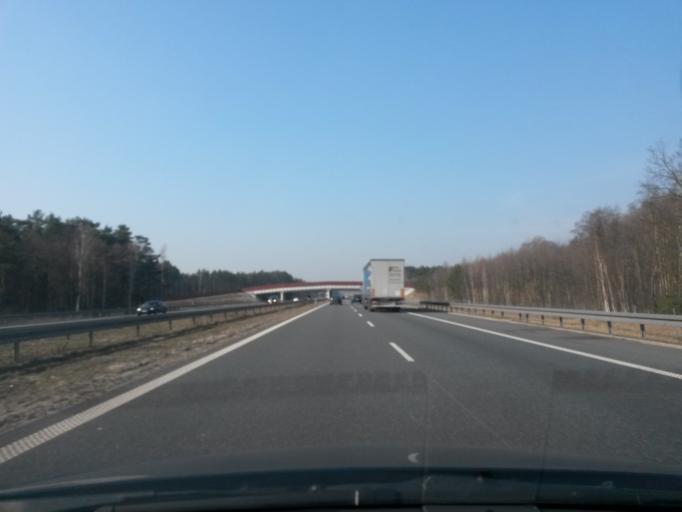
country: PL
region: Lodz Voivodeship
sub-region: Powiat skierniewicki
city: Bolimow
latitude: 52.0549
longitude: 20.1277
